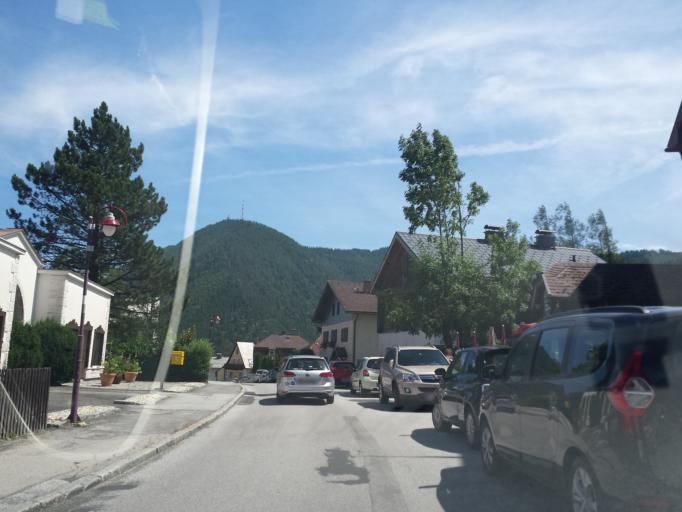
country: AT
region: Lower Austria
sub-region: Politischer Bezirk Neunkirchen
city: Semmering
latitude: 47.6350
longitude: 15.8279
